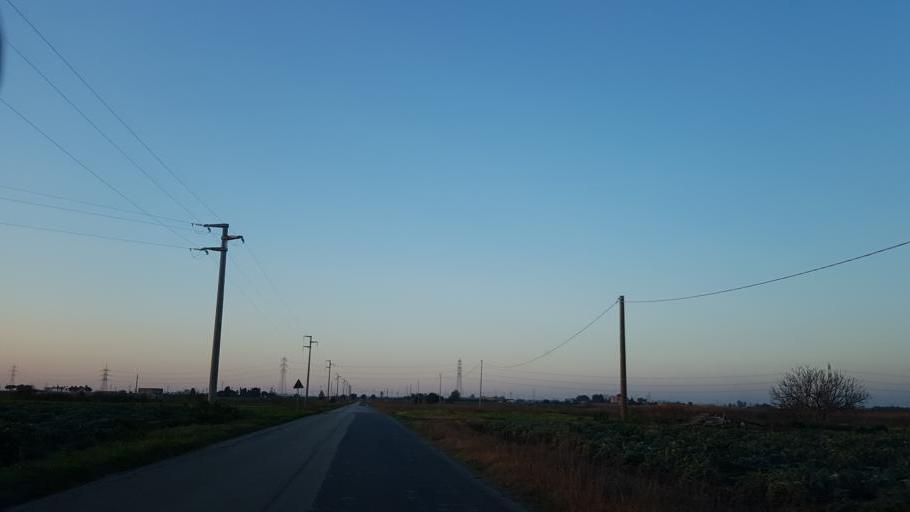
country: IT
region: Apulia
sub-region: Provincia di Brindisi
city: La Rosa
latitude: 40.5842
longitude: 17.9474
